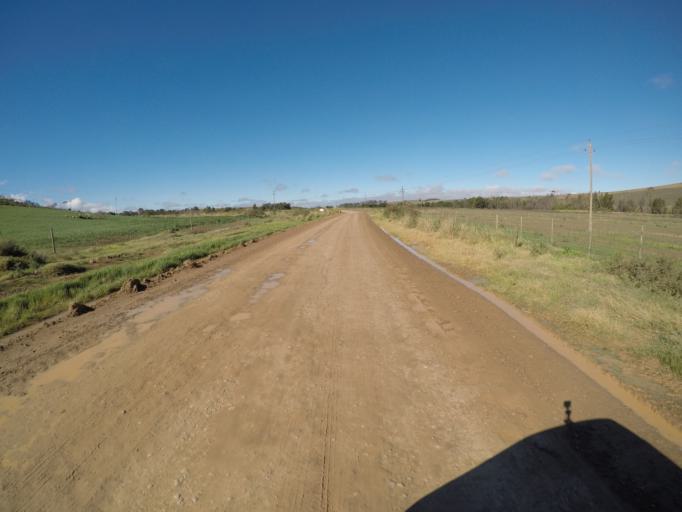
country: ZA
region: Western Cape
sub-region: Overberg District Municipality
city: Caledon
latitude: -34.0920
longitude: 19.6637
